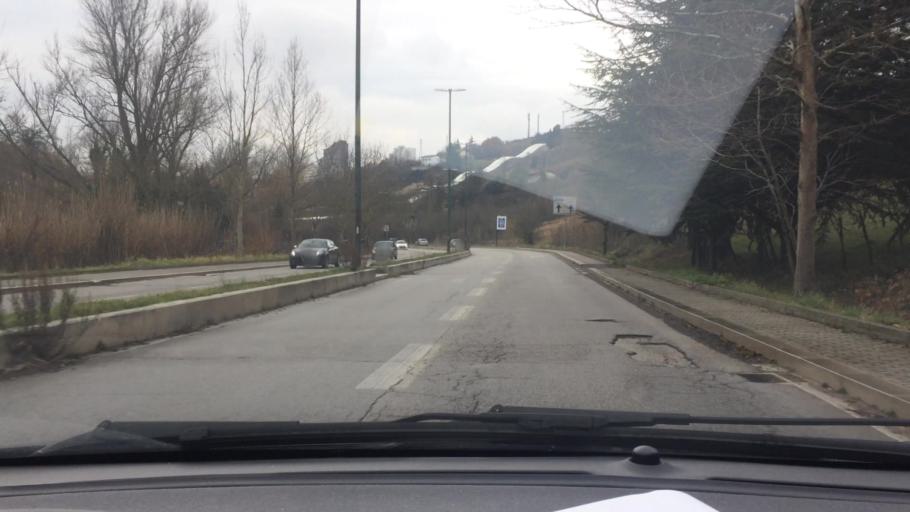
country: IT
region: Basilicate
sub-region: Provincia di Potenza
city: Potenza
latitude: 40.6404
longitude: 15.7980
